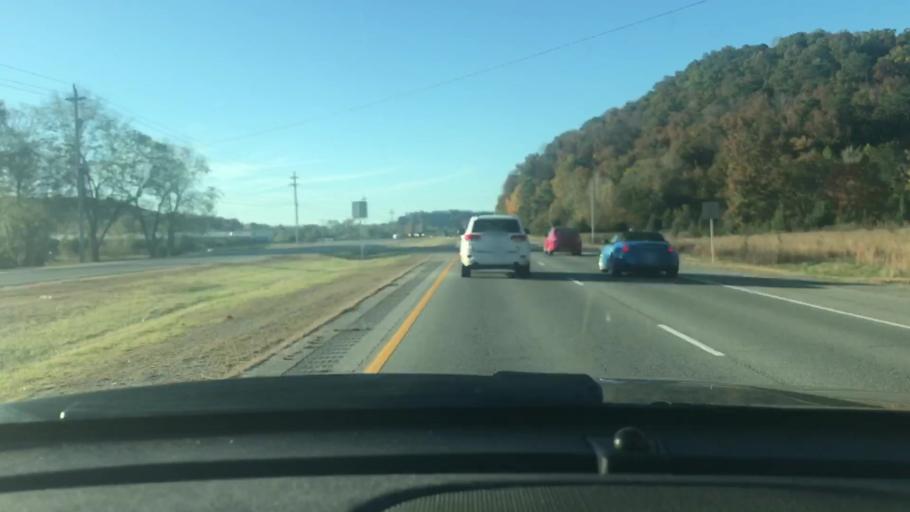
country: US
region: Tennessee
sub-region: Cheatham County
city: Ashland City
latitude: 36.2465
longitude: -87.0280
